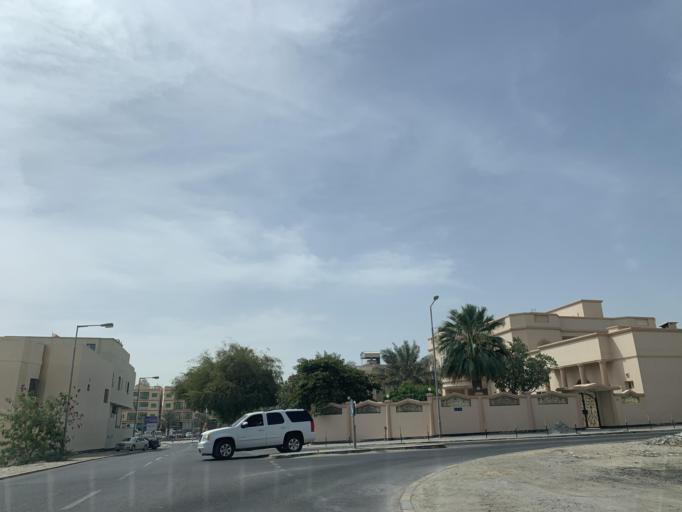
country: BH
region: Northern
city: Ar Rifa'
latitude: 26.1403
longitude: 50.5763
